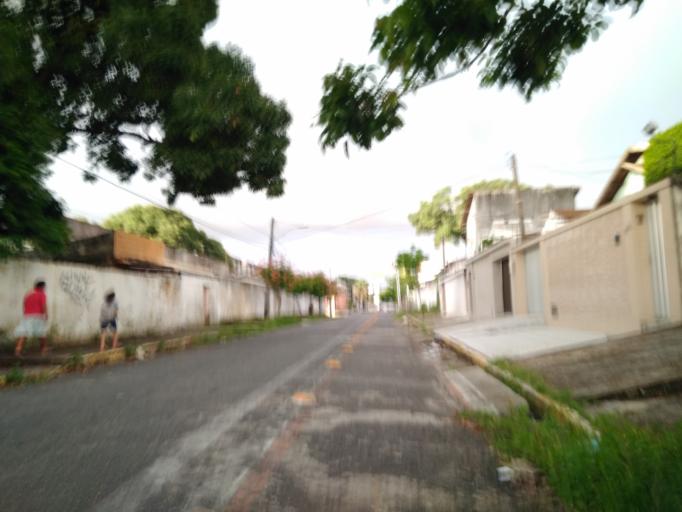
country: BR
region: Pernambuco
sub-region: Recife
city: Recife
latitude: -8.0352
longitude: -34.8898
